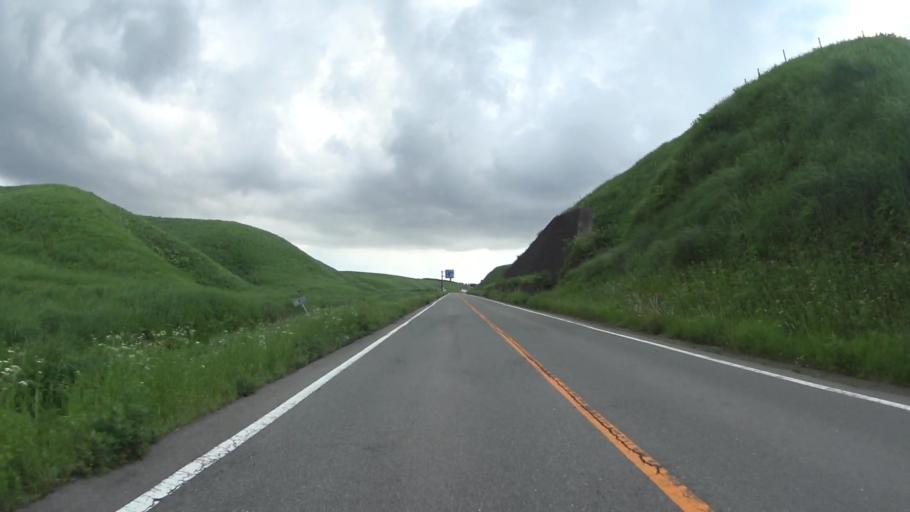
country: JP
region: Kumamoto
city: Aso
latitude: 33.0039
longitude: 131.1407
